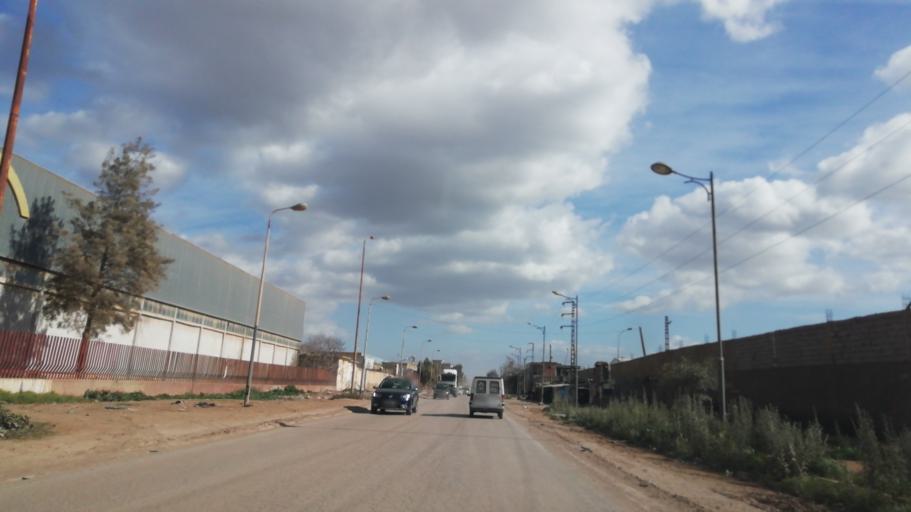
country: DZ
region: Oran
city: Es Senia
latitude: 35.6510
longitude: -0.5888
